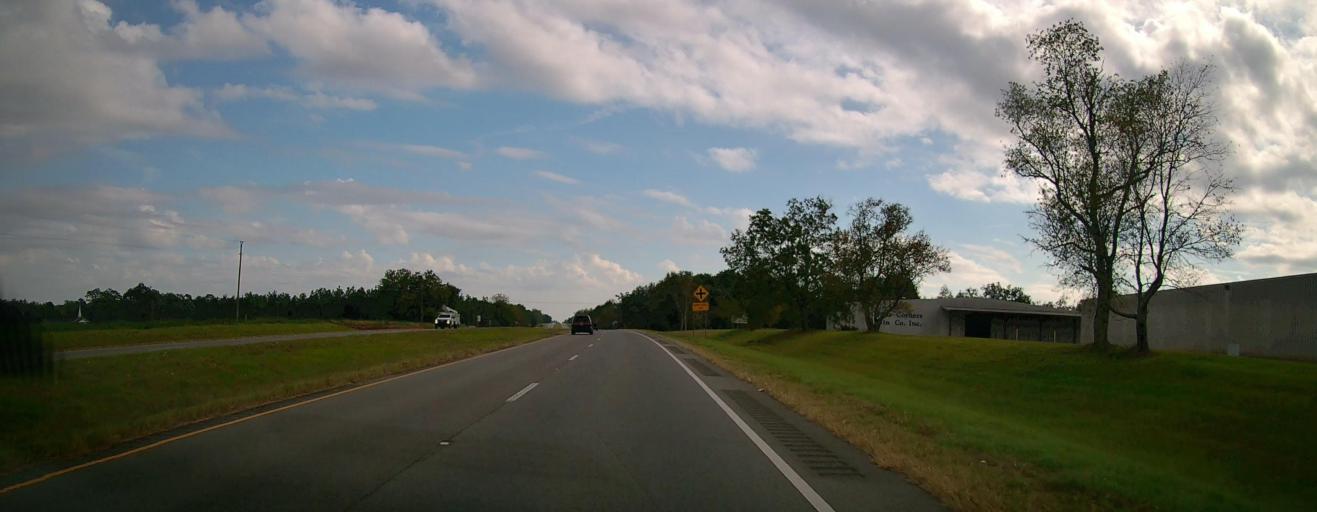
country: US
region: Georgia
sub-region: Thomas County
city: Meigs
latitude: 31.0462
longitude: -84.0702
